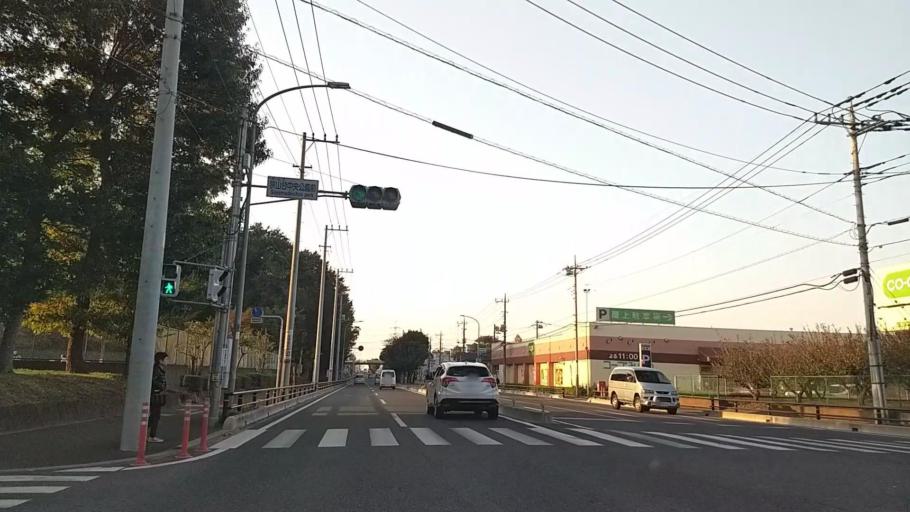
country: JP
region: Saitama
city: Sayama
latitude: 35.8546
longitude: 139.4352
